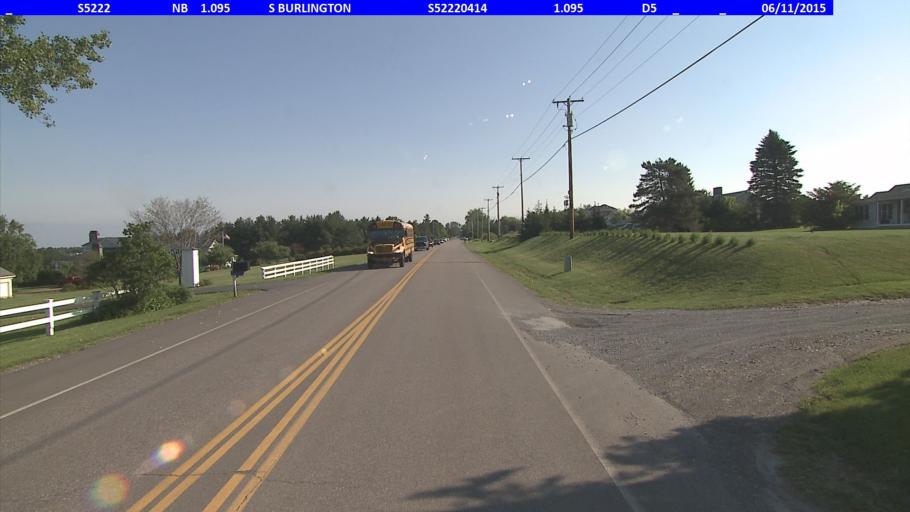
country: US
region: Vermont
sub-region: Chittenden County
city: South Burlington
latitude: 44.4325
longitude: -73.1926
